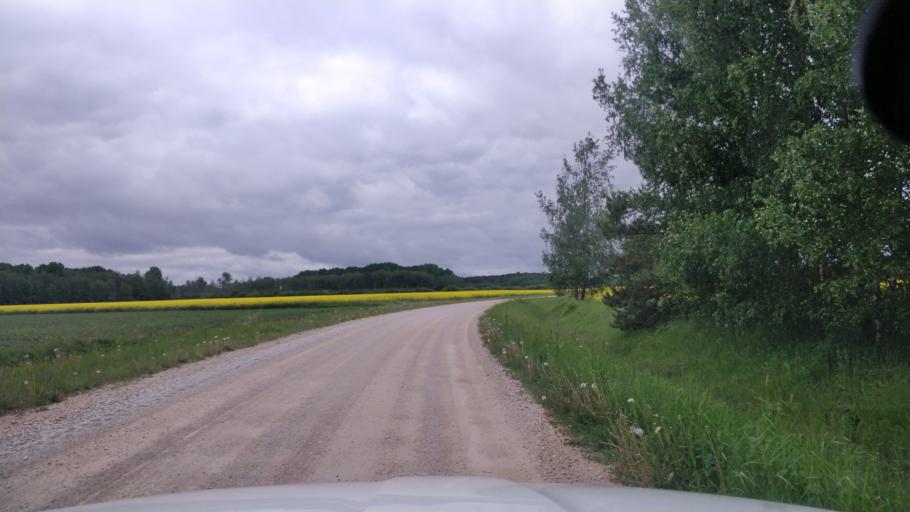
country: EE
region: Paernumaa
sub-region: Halinga vald
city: Parnu-Jaagupi
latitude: 58.7091
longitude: 24.3421
